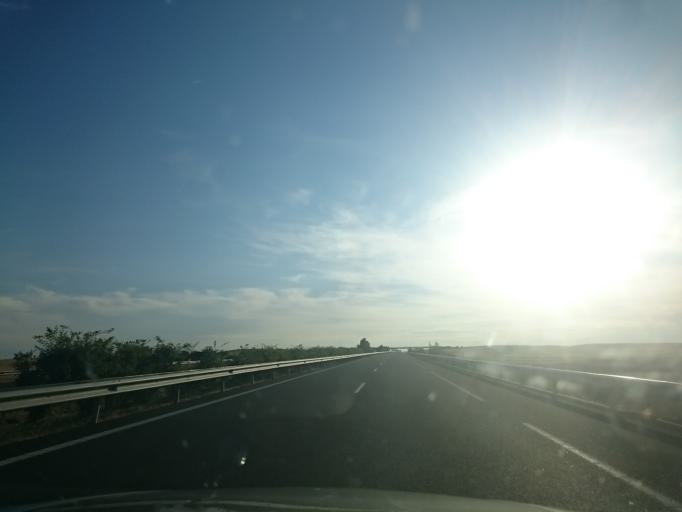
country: ES
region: Castille and Leon
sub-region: Provincia de Palencia
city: Moratinos
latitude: 42.3636
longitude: -4.9168
